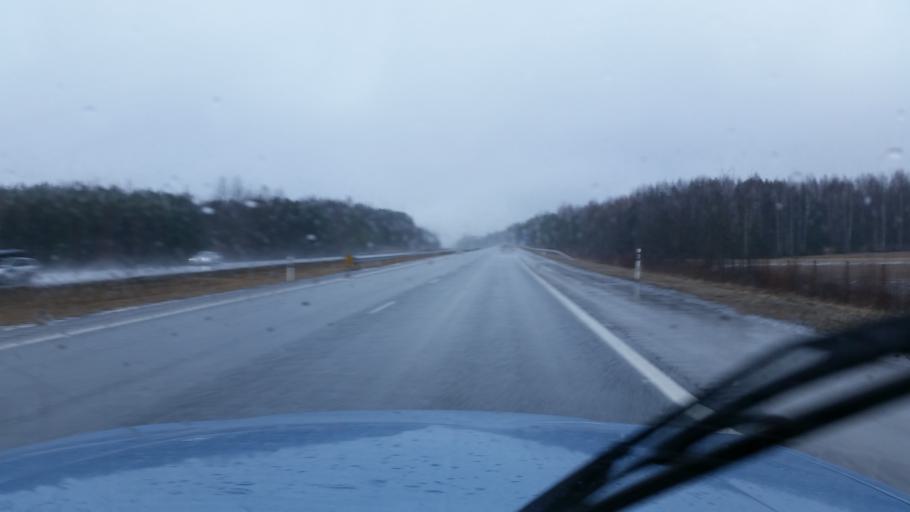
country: FI
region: Haeme
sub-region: Haemeenlinna
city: Tervakoski
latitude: 60.8076
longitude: 24.6802
